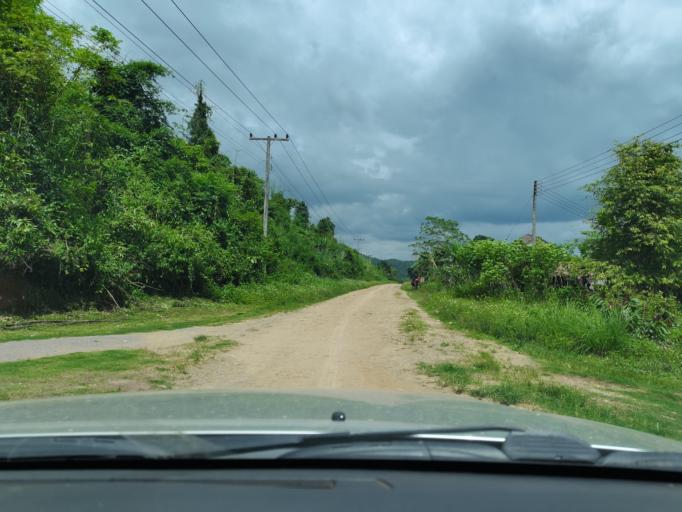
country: LA
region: Loungnamtha
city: Muang Long
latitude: 20.6807
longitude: 101.0550
